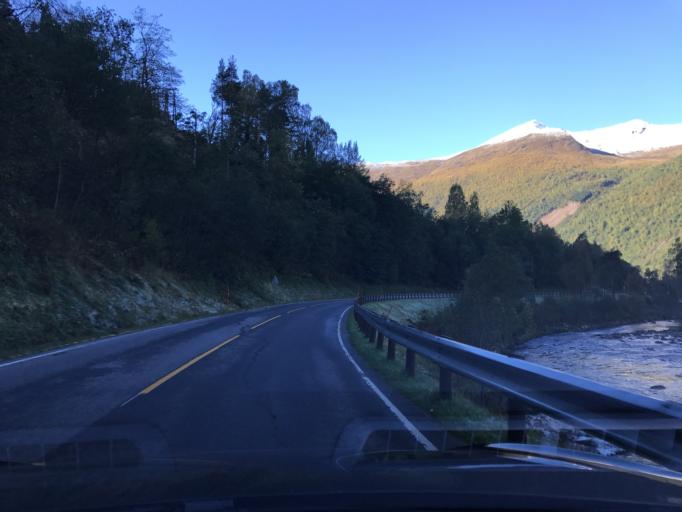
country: NO
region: More og Romsdal
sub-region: Norddal
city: Valldal
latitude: 62.3123
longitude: 7.2892
